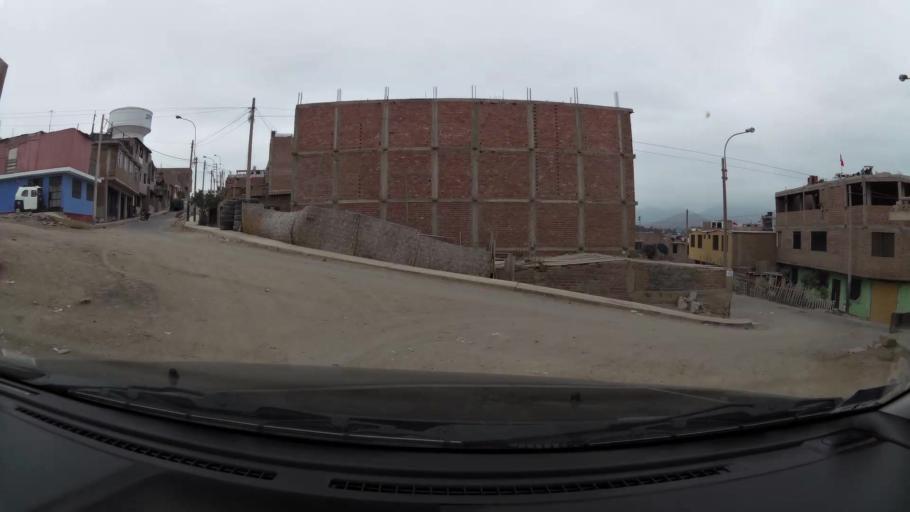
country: PE
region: Lima
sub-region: Lima
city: Surco
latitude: -12.1940
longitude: -76.9768
